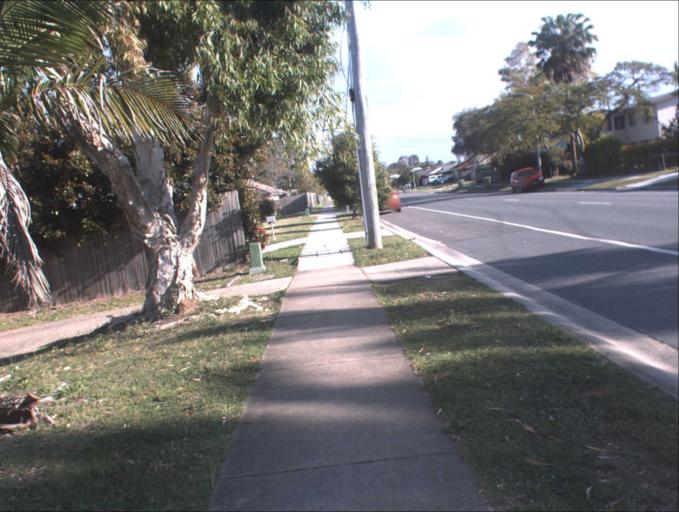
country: AU
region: Queensland
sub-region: Logan
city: Logan City
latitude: -27.6743
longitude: 153.0857
